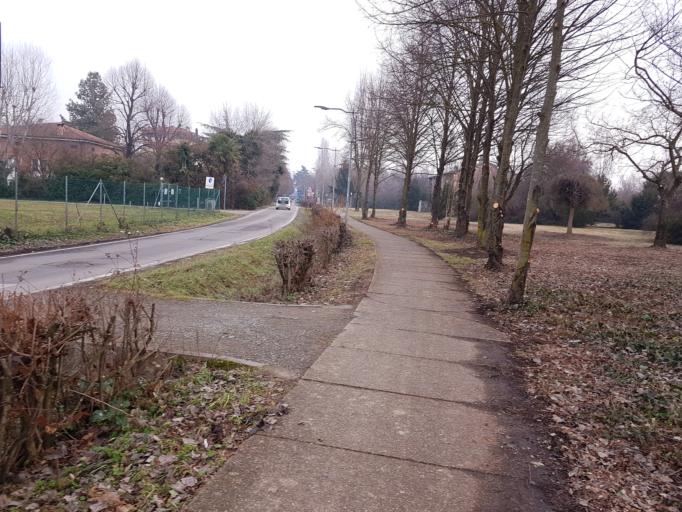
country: IT
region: Emilia-Romagna
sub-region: Provincia di Bologna
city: Quarto Inferiore
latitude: 44.5086
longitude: 11.3861
